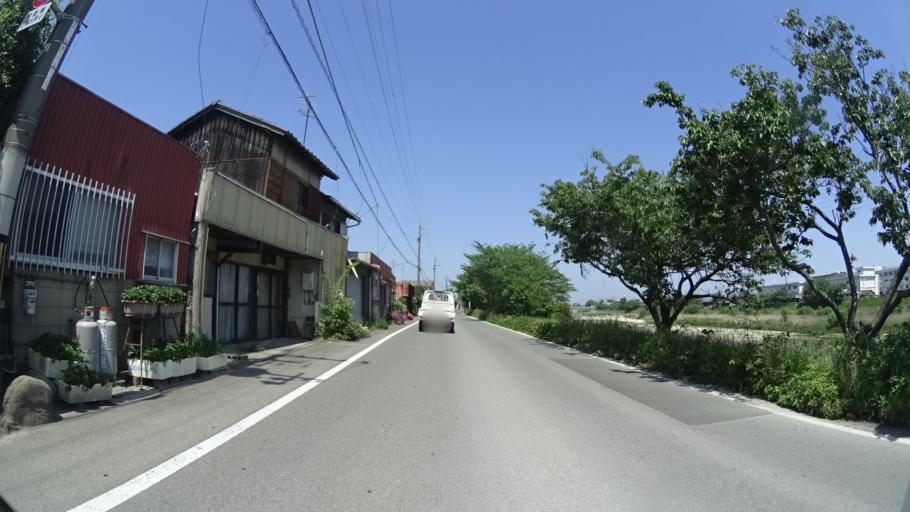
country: JP
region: Ehime
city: Hojo
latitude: 34.0522
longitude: 132.9919
